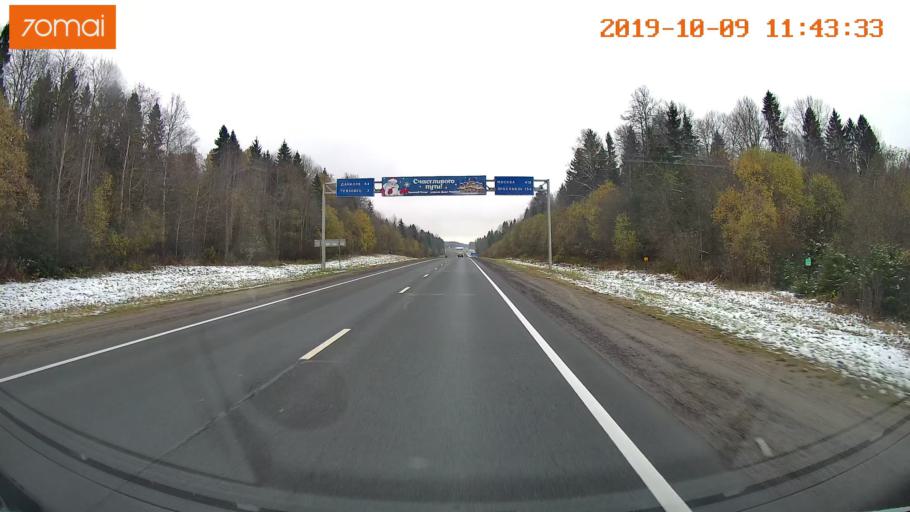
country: RU
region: Vologda
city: Gryazovets
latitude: 58.8952
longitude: 40.1862
